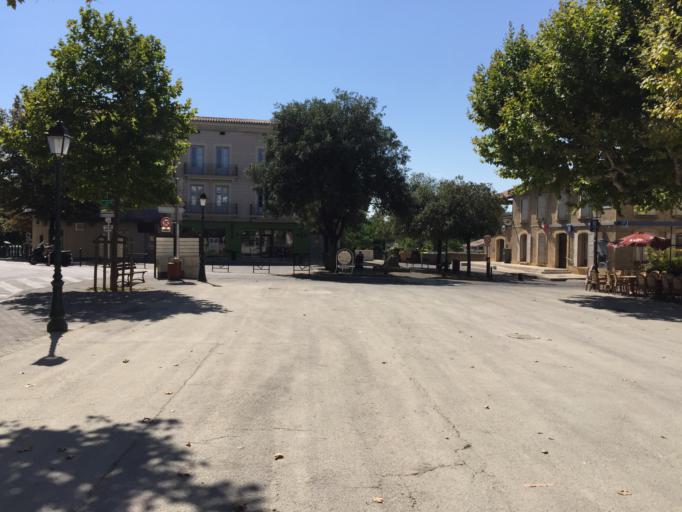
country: FR
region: Provence-Alpes-Cote d'Azur
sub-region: Departement des Alpes-de-Haute-Provence
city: Forcalquier
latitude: 43.9598
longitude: 5.7810
